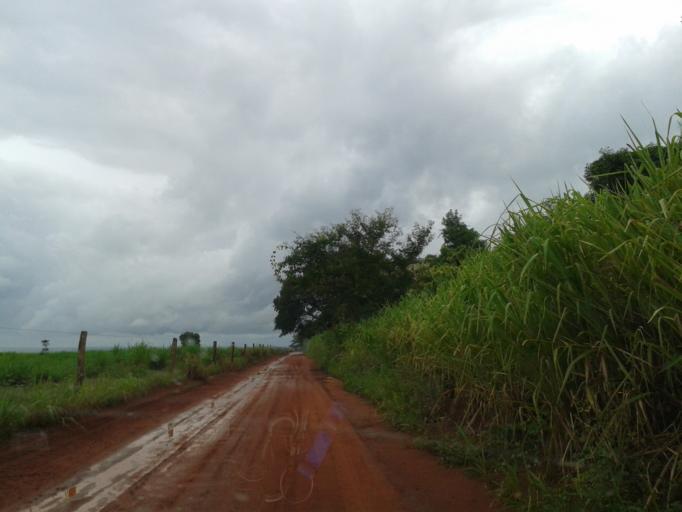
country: BR
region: Minas Gerais
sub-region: Santa Vitoria
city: Santa Vitoria
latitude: -18.7209
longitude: -49.9672
